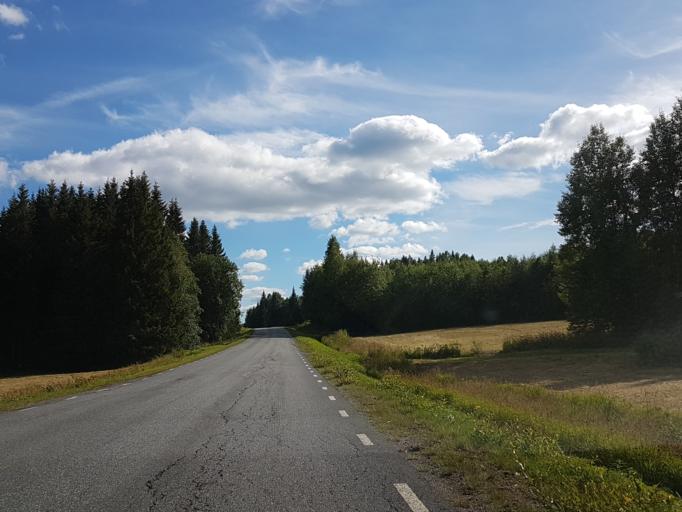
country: SE
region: Vaesterbotten
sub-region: Skelleftea Kommun
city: Burtraesk
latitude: 64.3166
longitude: 20.5315
